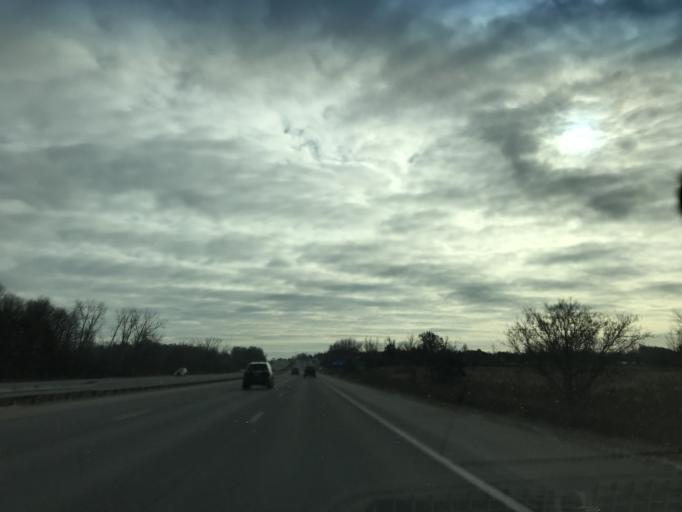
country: US
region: Michigan
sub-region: Oakland County
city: Waterford
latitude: 42.7149
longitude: -83.3412
